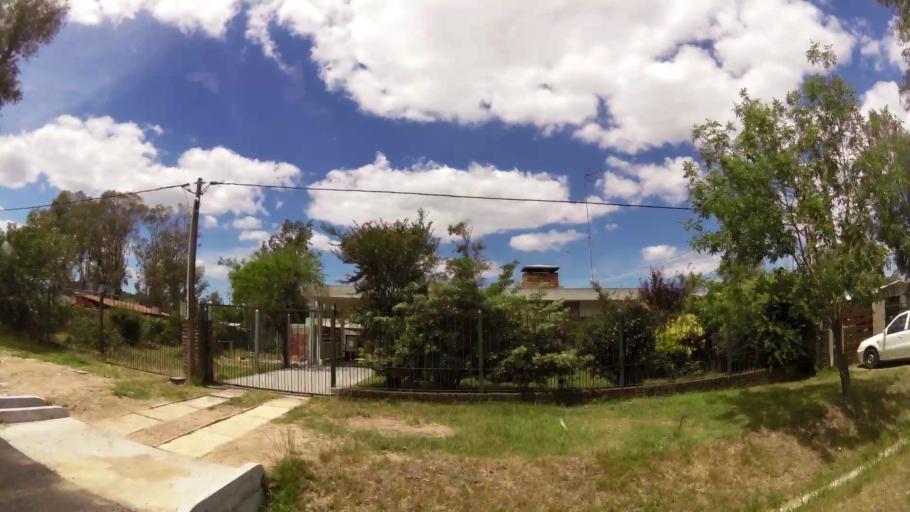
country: UY
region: Canelones
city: Colonia Nicolich
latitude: -34.8255
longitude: -55.9688
